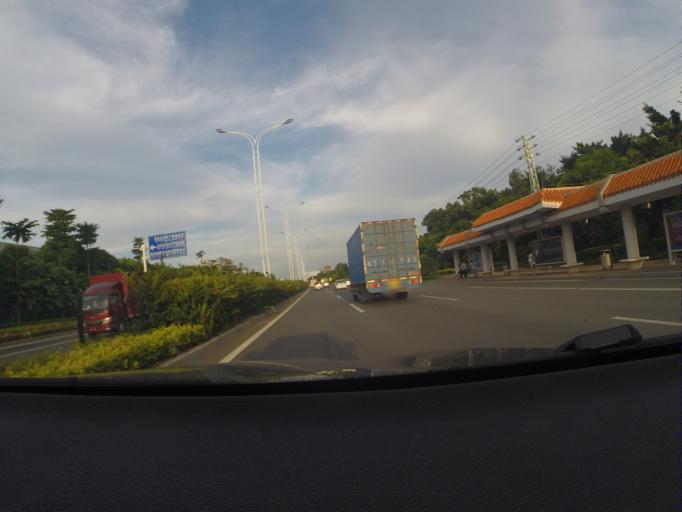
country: CN
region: Guangdong
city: Tangjiawan
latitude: 22.3769
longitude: 113.5542
